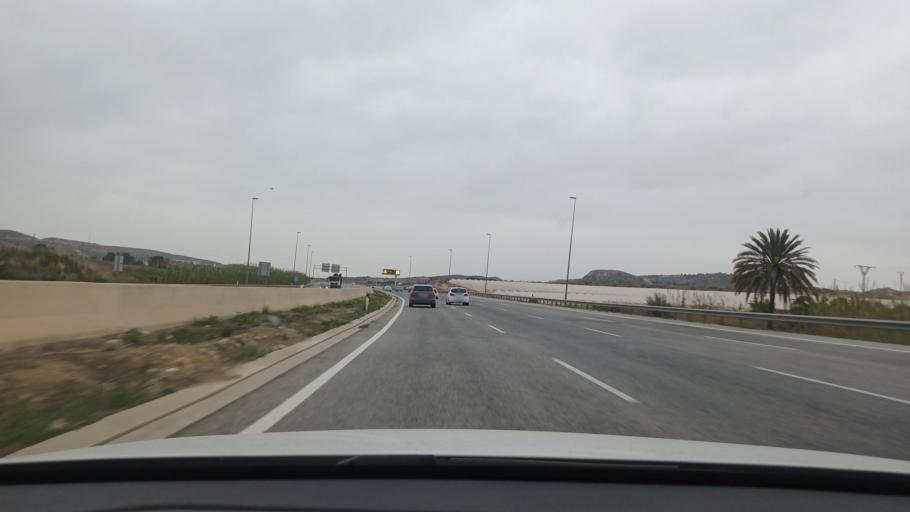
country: ES
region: Valencia
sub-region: Provincia de Alicante
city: Monforte del Cid
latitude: 38.3347
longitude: -0.6639
